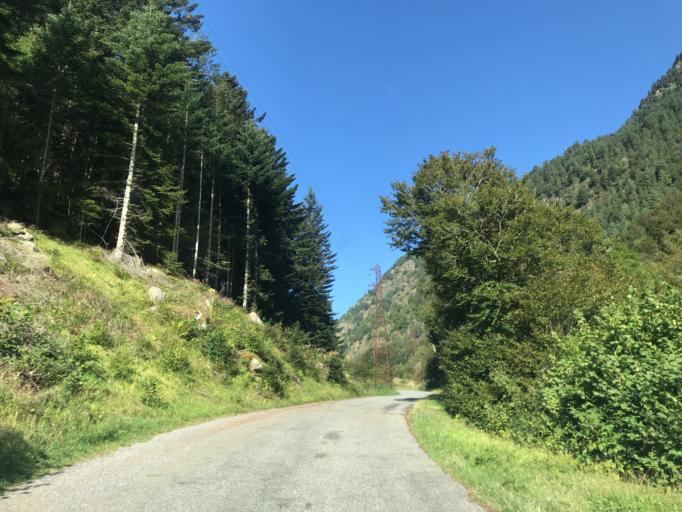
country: FR
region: Midi-Pyrenees
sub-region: Departement des Hautes-Pyrenees
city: Saint-Lary-Soulan
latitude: 42.8137
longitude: 0.2169
